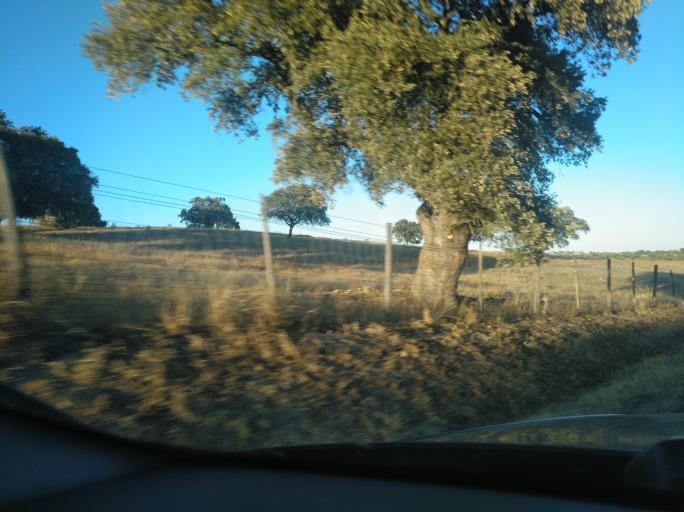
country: PT
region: Portalegre
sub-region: Arronches
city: Arronches
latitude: 39.0682
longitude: -7.2247
